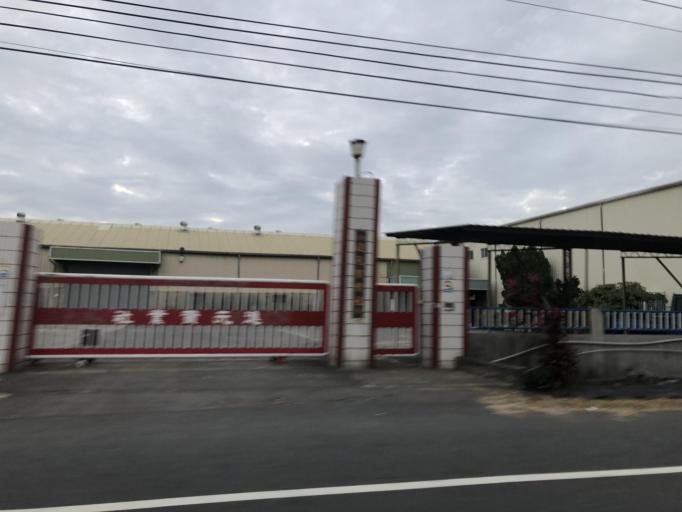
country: TW
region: Taiwan
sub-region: Tainan
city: Tainan
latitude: 23.0259
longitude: 120.2958
